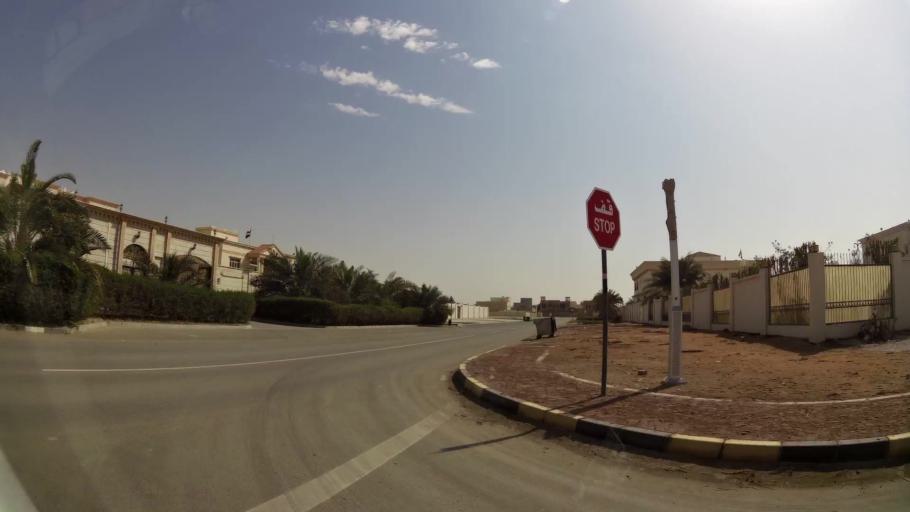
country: AE
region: Abu Dhabi
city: Abu Dhabi
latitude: 24.3321
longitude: 54.5476
